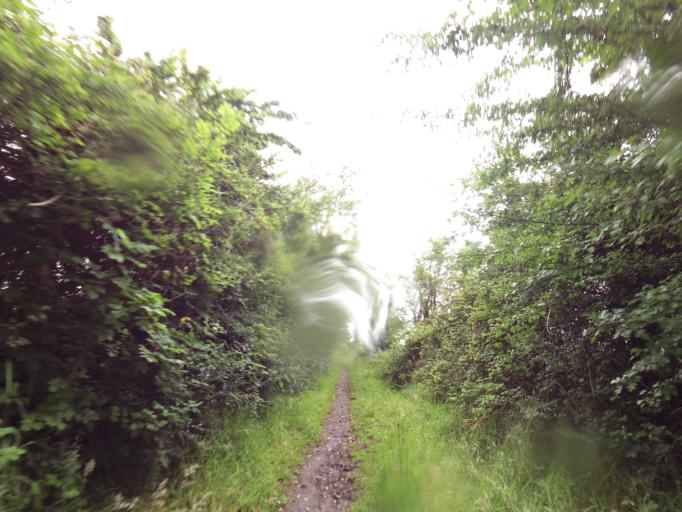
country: IE
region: Connaught
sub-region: County Galway
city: Athenry
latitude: 53.2856
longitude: -8.7082
